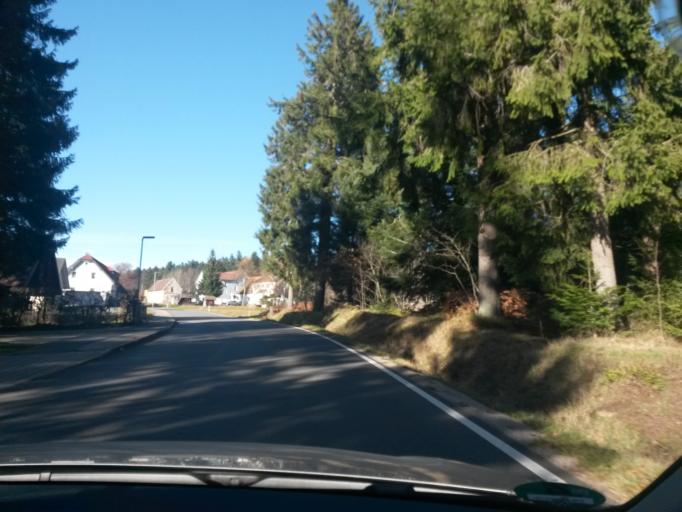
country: DE
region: Baden-Wuerttemberg
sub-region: Karlsruhe Region
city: Bad Rippoldsau-Schapbach
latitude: 48.4715
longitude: 8.2994
